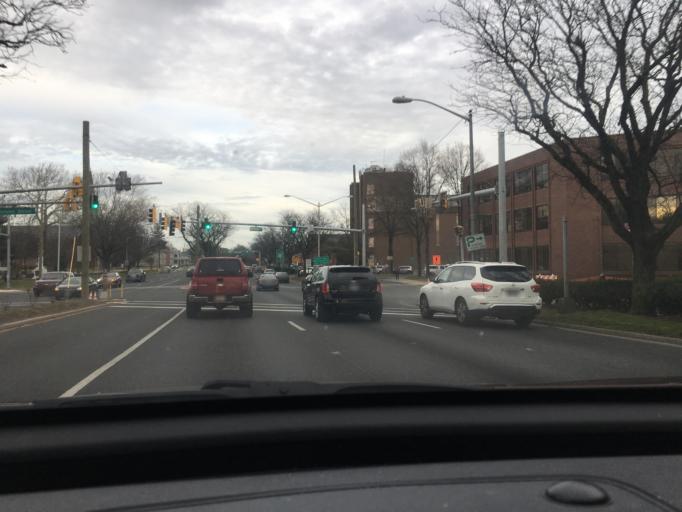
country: US
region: Maryland
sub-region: Wicomico County
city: Salisbury
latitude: 38.3665
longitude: -75.6009
